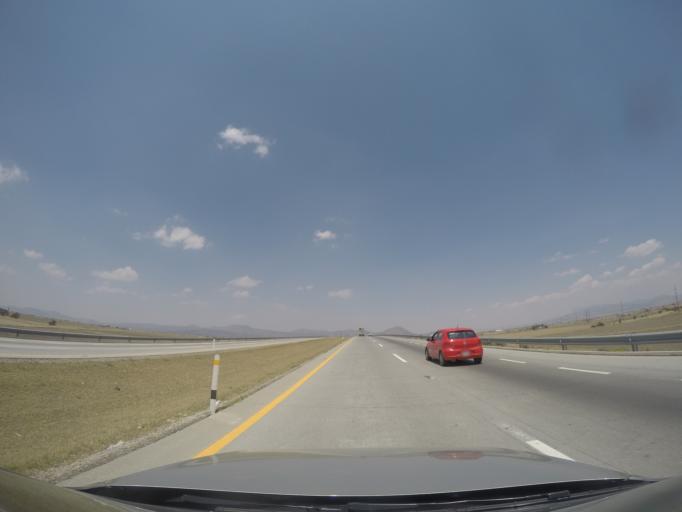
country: MX
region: Hidalgo
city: Calpulalpan
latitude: 19.6096
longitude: -98.5393
